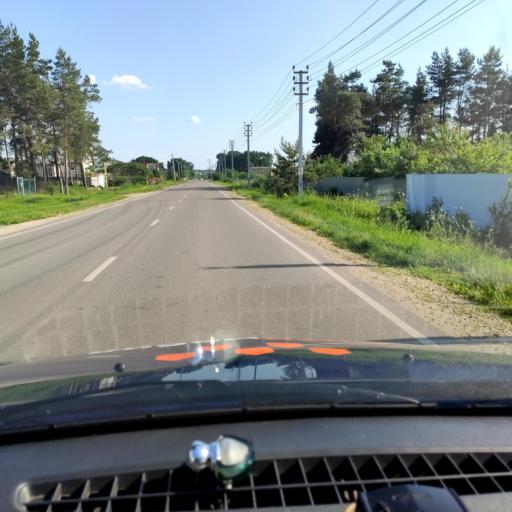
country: RU
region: Voronezj
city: Podgornoye
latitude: 51.8766
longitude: 39.1733
